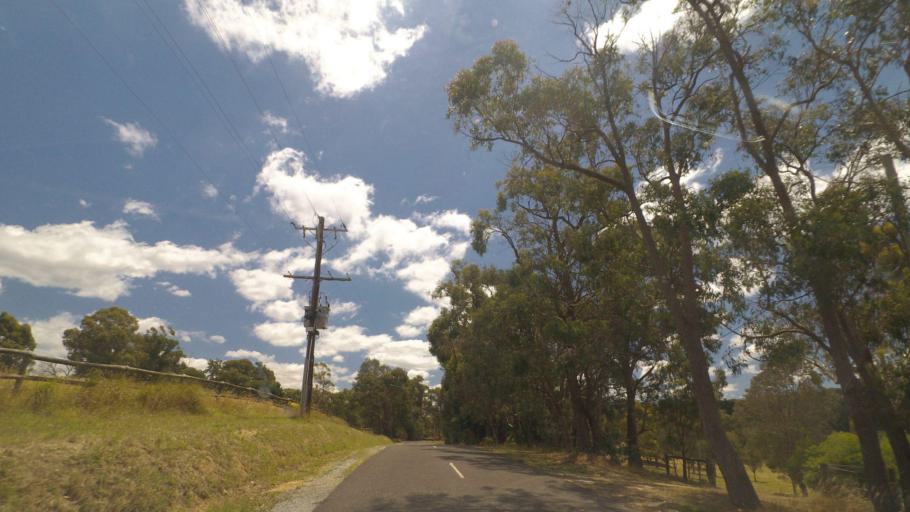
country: AU
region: Victoria
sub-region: Yarra Ranges
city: Chirnside Park
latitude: -37.7274
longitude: 145.2726
